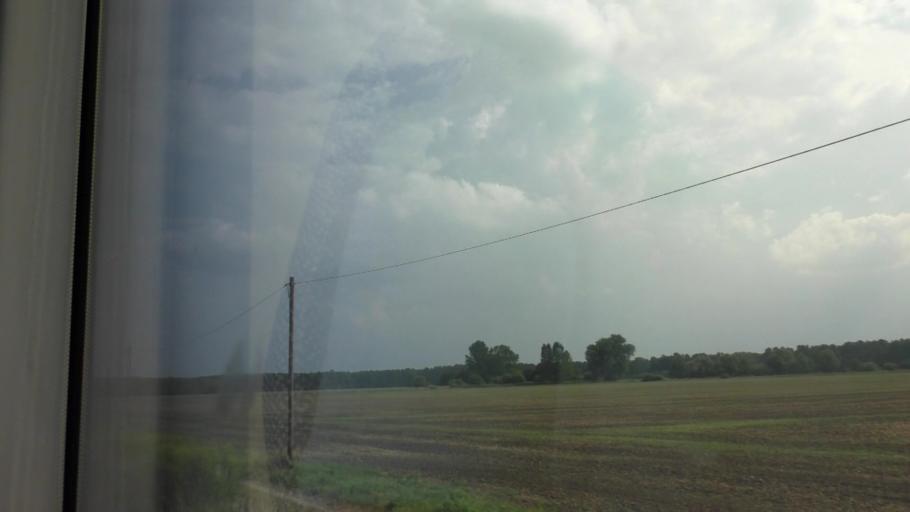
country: DE
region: Brandenburg
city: Erkner
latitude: 52.2931
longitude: 13.7748
